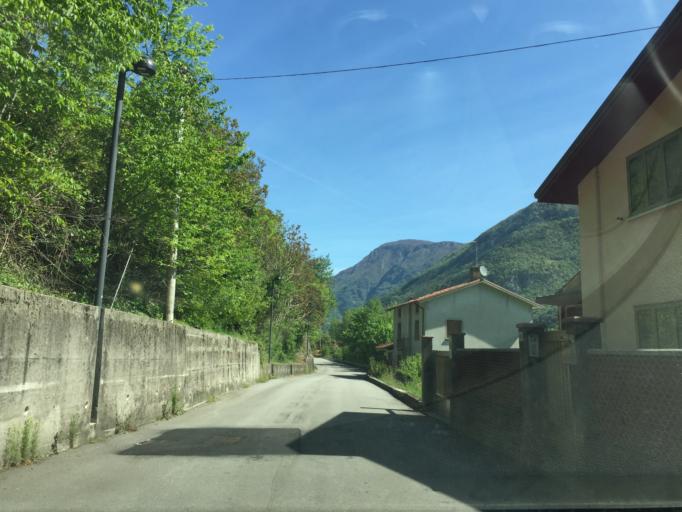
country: IT
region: Friuli Venezia Giulia
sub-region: Provincia di Udine
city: Trasaghis
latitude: 46.2949
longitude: 13.0500
